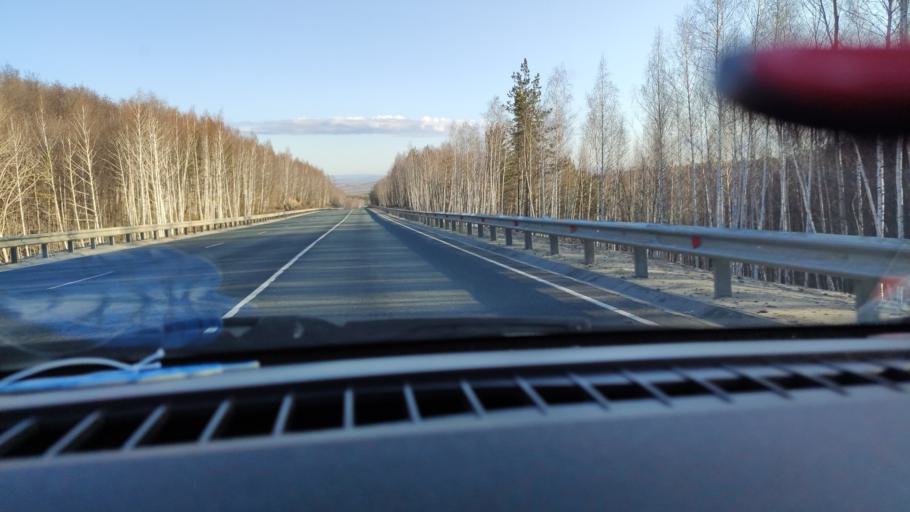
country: RU
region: Saratov
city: Khvalynsk
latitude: 52.4998
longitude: 48.0148
